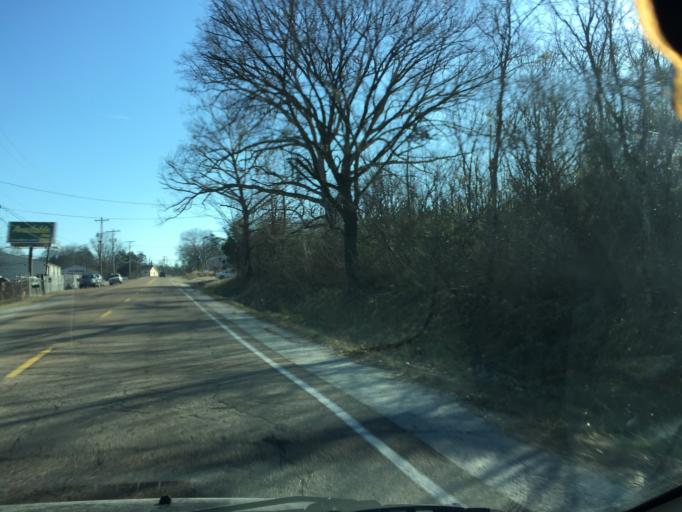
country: US
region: Tennessee
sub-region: Hamilton County
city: Harrison
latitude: 35.0703
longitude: -85.1122
